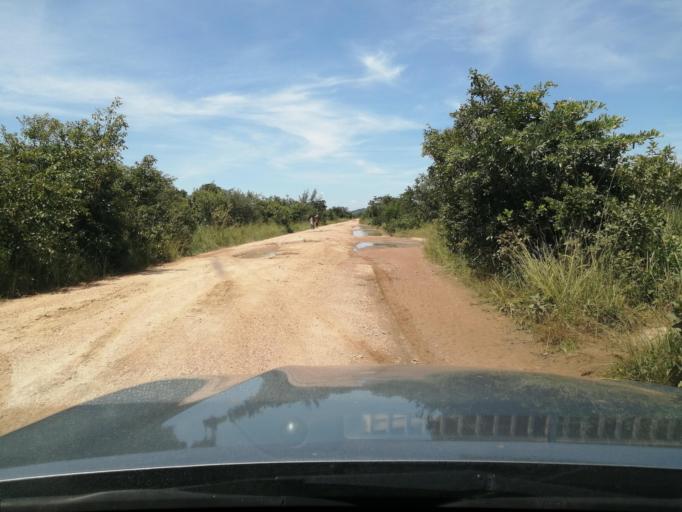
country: ZM
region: Central
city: Chibombo
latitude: -15.0468
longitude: 27.8245
